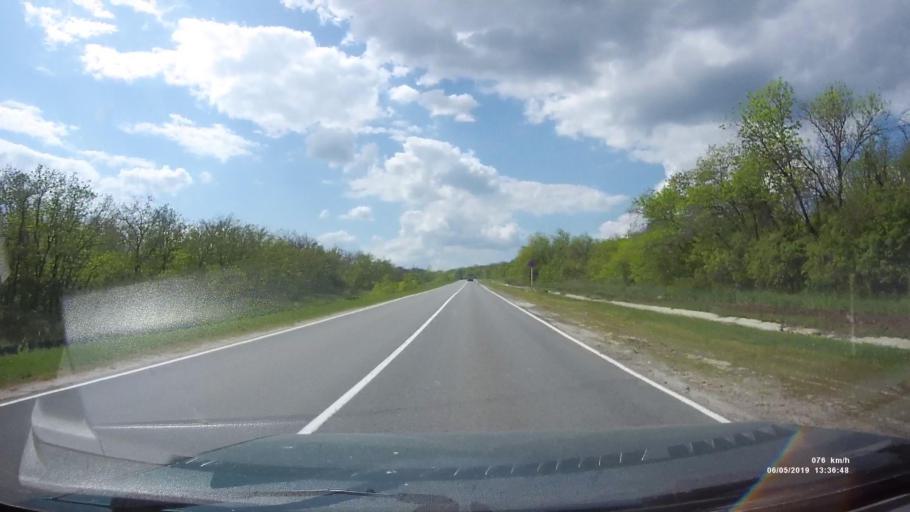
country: RU
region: Rostov
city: Ust'-Donetskiy
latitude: 47.6893
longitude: 40.7262
